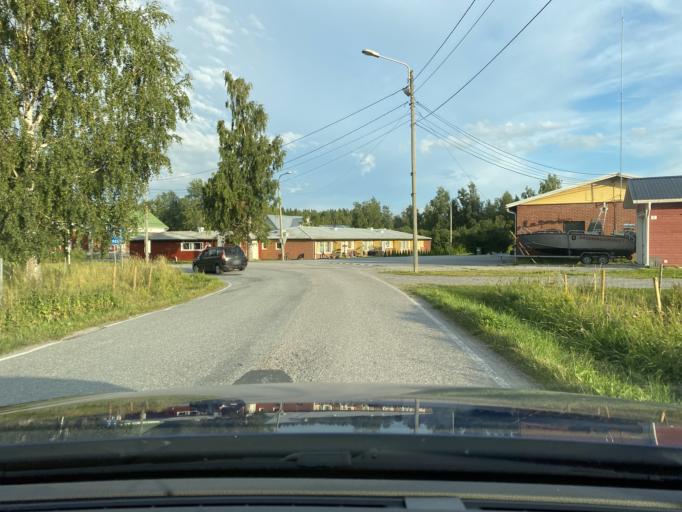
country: FI
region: Ostrobothnia
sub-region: Vaasa
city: Korsnaes
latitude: 62.9691
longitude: 21.1907
